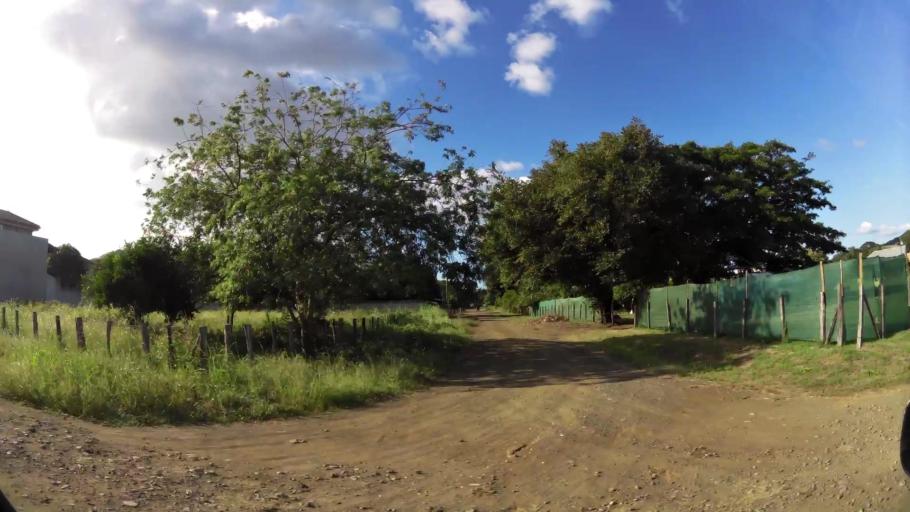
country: CR
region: Guanacaste
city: Sardinal
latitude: 10.5464
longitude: -85.6971
